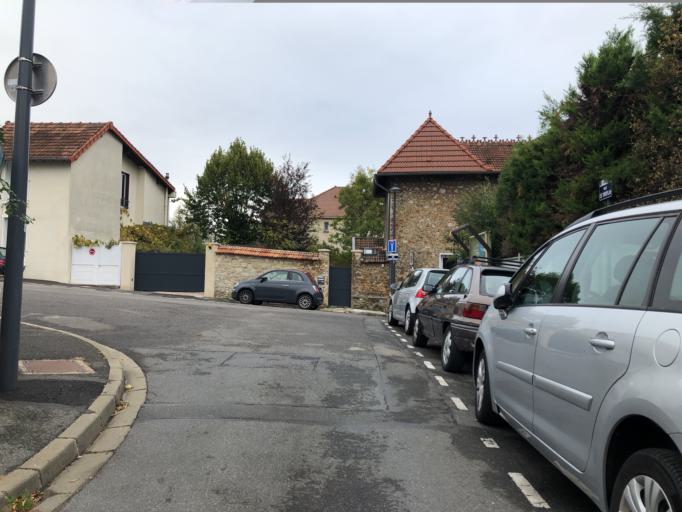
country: FR
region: Ile-de-France
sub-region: Departement des Hauts-de-Seine
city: Chaville
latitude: 48.8068
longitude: 2.1831
